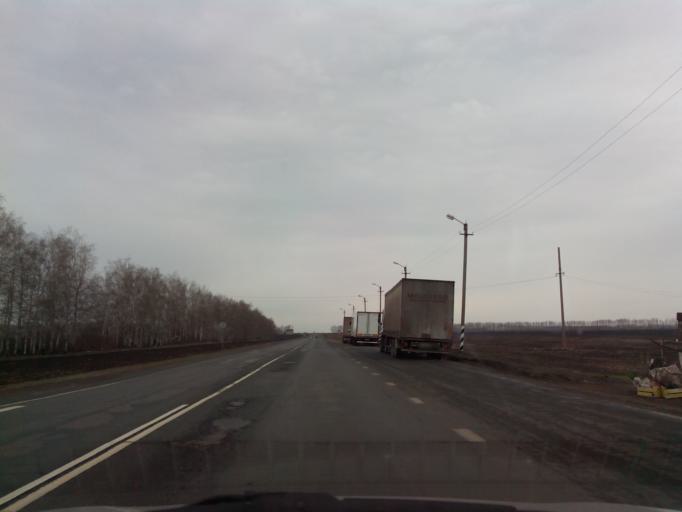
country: RU
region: Tambov
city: Zavoronezhskoye
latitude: 52.9779
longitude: 40.5669
